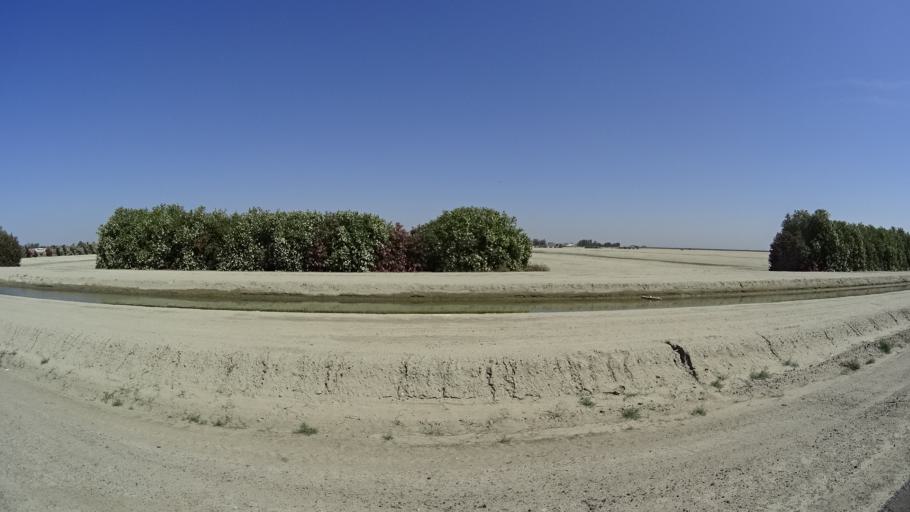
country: US
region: California
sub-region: Kings County
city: Corcoran
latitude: 36.0725
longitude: -119.5526
